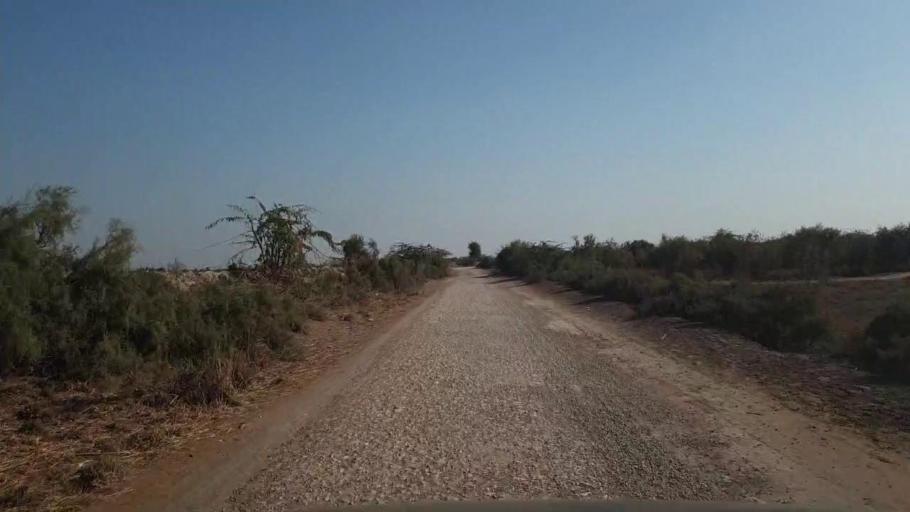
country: PK
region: Sindh
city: Shahpur Chakar
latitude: 26.1514
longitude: 68.6772
